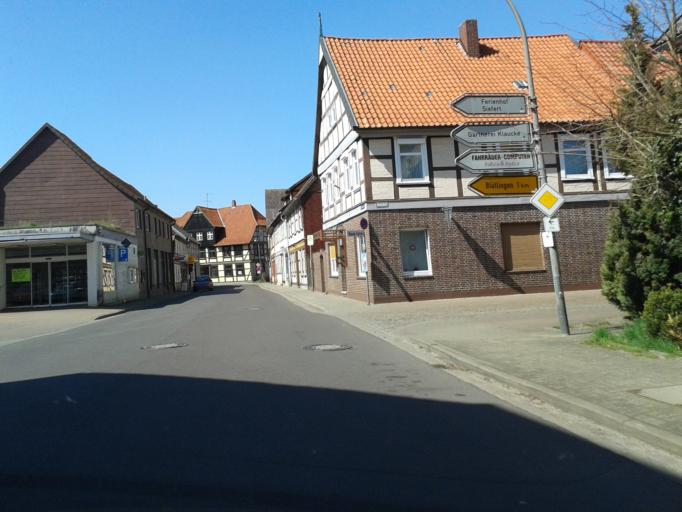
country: DE
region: Lower Saxony
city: Wustrow
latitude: 52.9242
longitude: 11.1202
